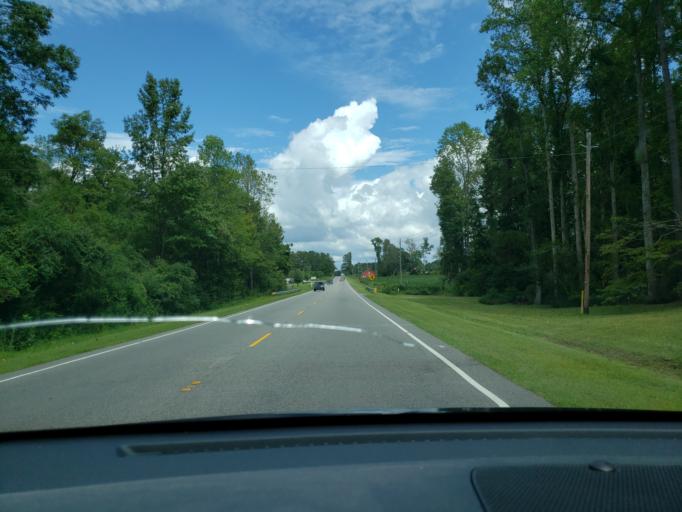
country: US
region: North Carolina
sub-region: Columbus County
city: Brunswick
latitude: 34.2234
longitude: -78.7550
